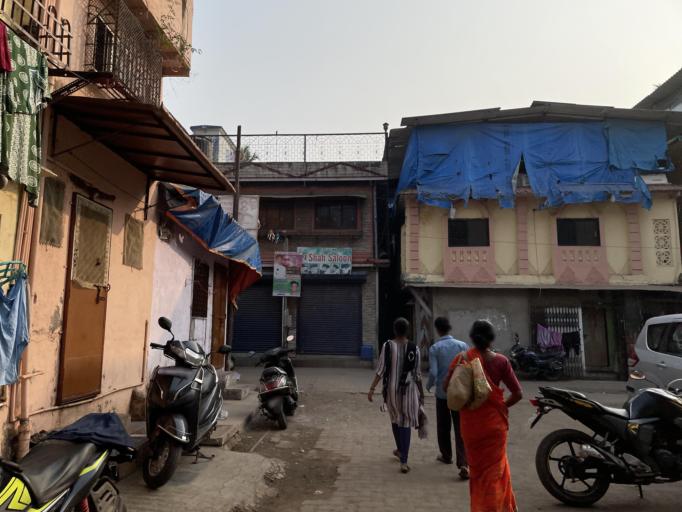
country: IN
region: Maharashtra
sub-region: Mumbai Suburban
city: Borivli
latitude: 19.1922
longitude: 72.8211
